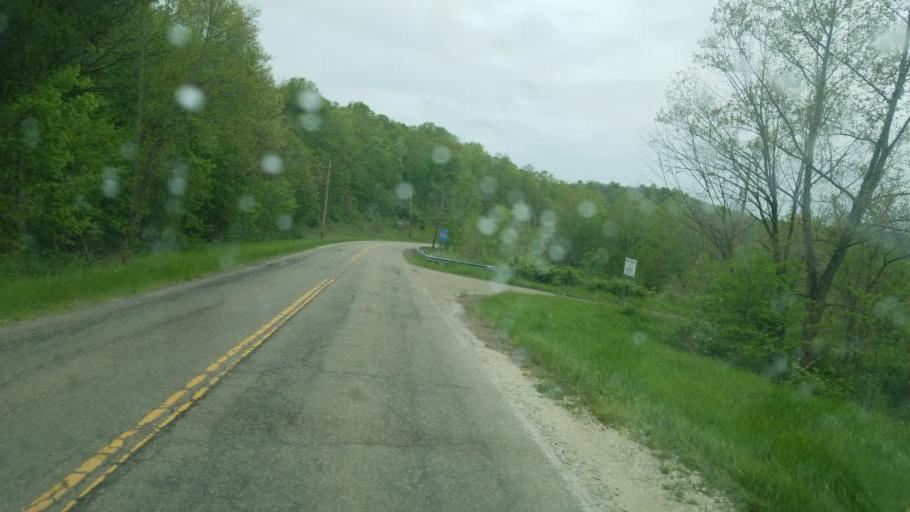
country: US
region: Ohio
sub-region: Guernsey County
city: Cambridge
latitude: 40.1466
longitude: -81.5459
